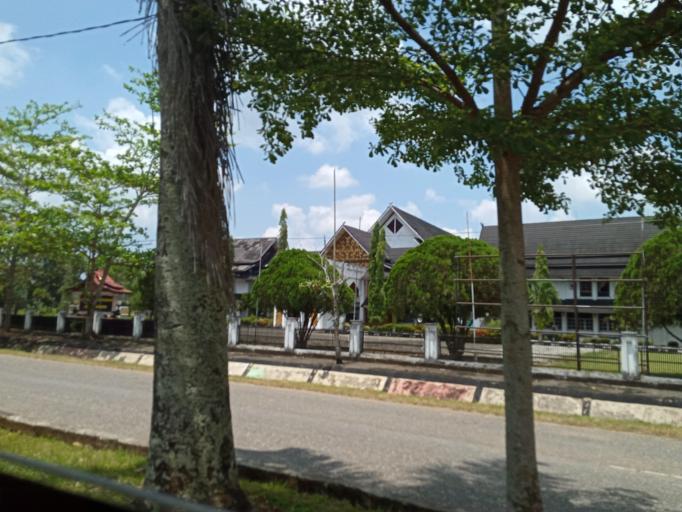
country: ID
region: Jambi
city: Bangko
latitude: -2.0573
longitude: 102.2794
